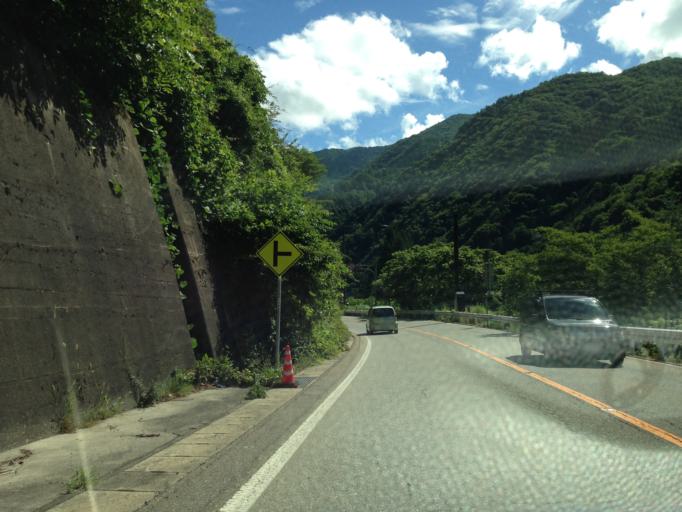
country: JP
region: Gifu
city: Takayama
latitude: 35.9937
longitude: 137.2784
